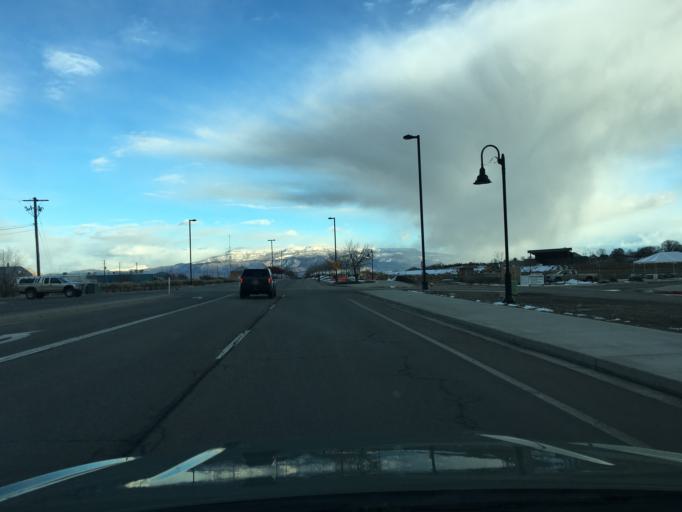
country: US
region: Colorado
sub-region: Mesa County
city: Grand Junction
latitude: 39.0559
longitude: -108.5583
